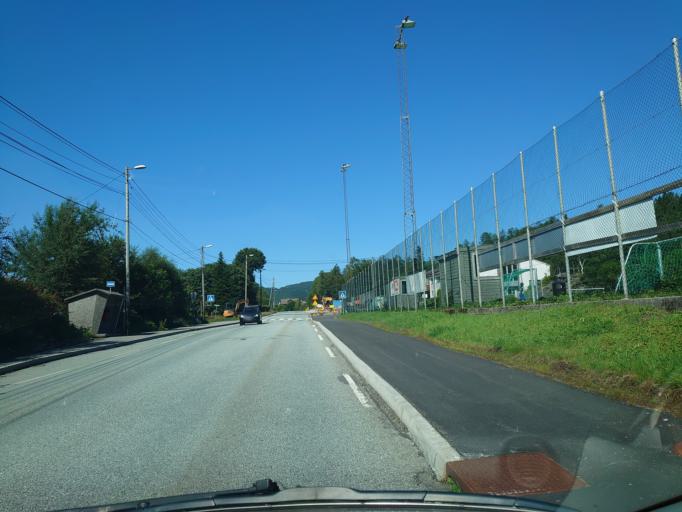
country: NO
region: Hordaland
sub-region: Bergen
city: Indre Arna
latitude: 60.4413
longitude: 5.4627
